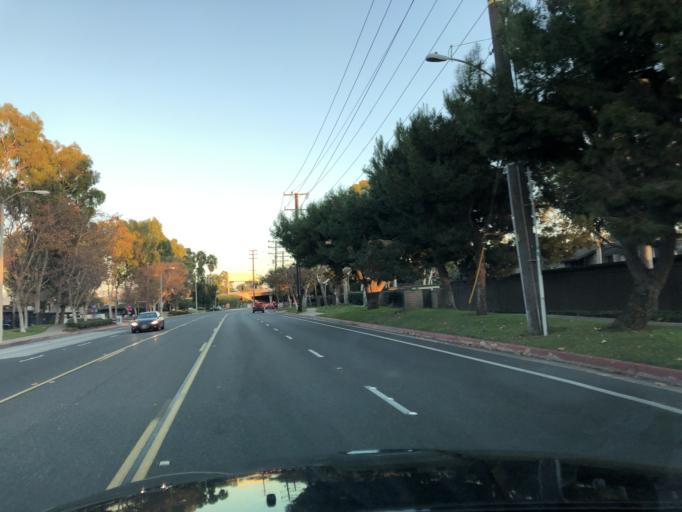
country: US
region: California
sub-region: Orange County
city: Costa Mesa
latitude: 33.6823
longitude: -117.8801
